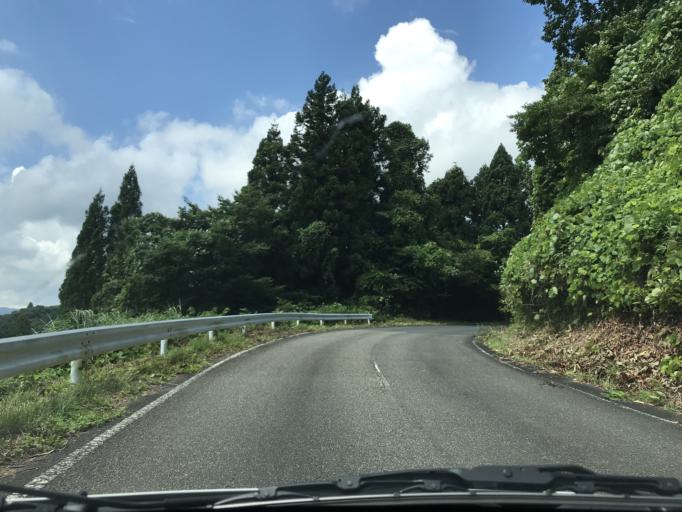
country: JP
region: Iwate
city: Mizusawa
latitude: 39.0610
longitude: 141.4023
